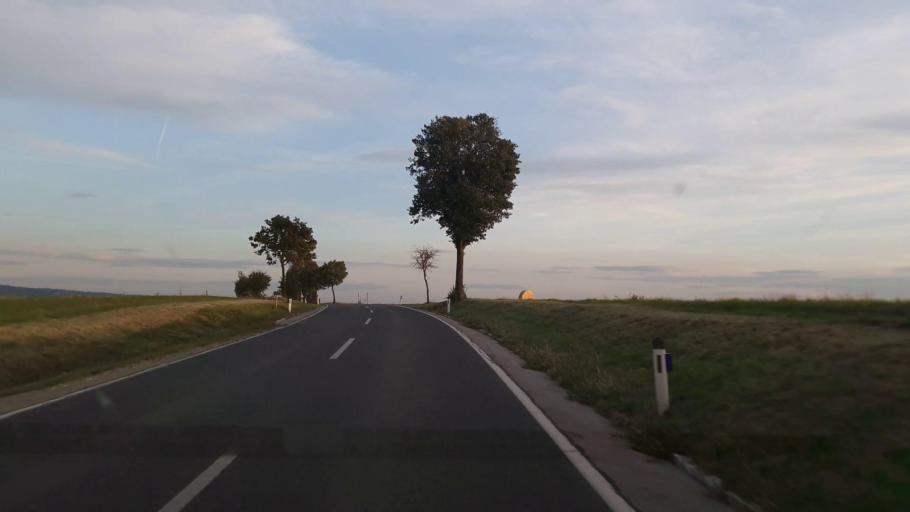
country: AT
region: Lower Austria
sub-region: Politischer Bezirk Korneuburg
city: Grossrussbach
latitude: 48.4407
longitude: 16.3896
